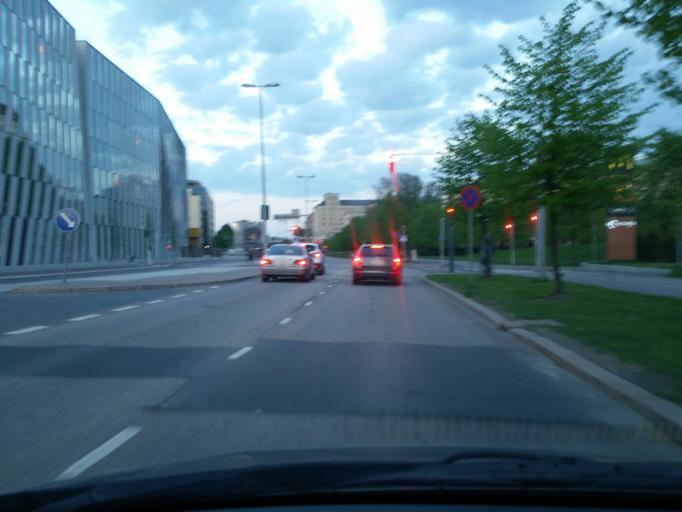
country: FI
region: Uusimaa
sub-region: Helsinki
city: Helsinki
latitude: 60.1906
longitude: 24.9564
